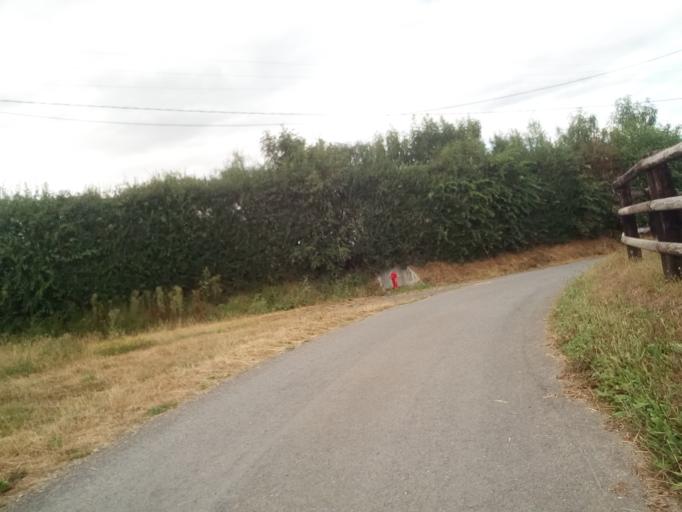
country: FR
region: Lower Normandy
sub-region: Departement du Calvados
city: Troarn
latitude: 49.1698
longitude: -0.1653
